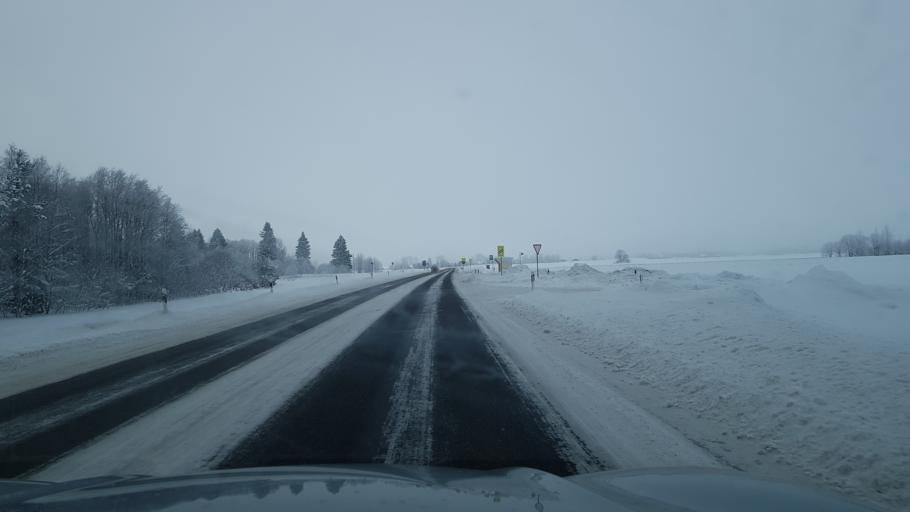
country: EE
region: Ida-Virumaa
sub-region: Johvi vald
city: Johvi
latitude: 59.3082
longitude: 27.3930
